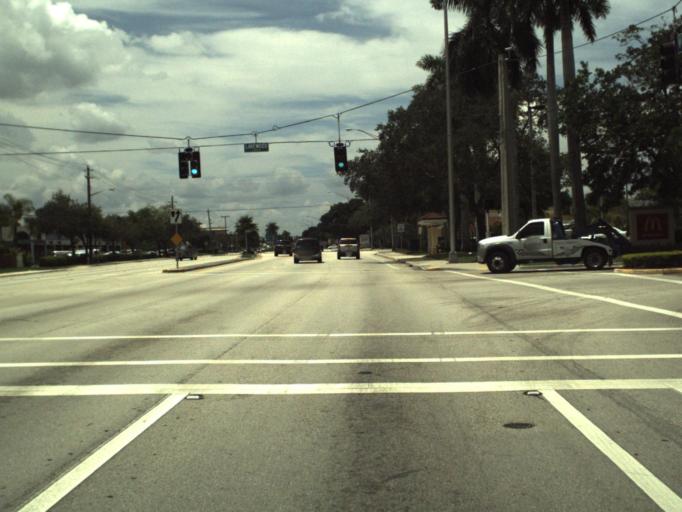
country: US
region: Florida
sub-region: Broward County
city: Margate
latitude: 26.2354
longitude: -80.1987
